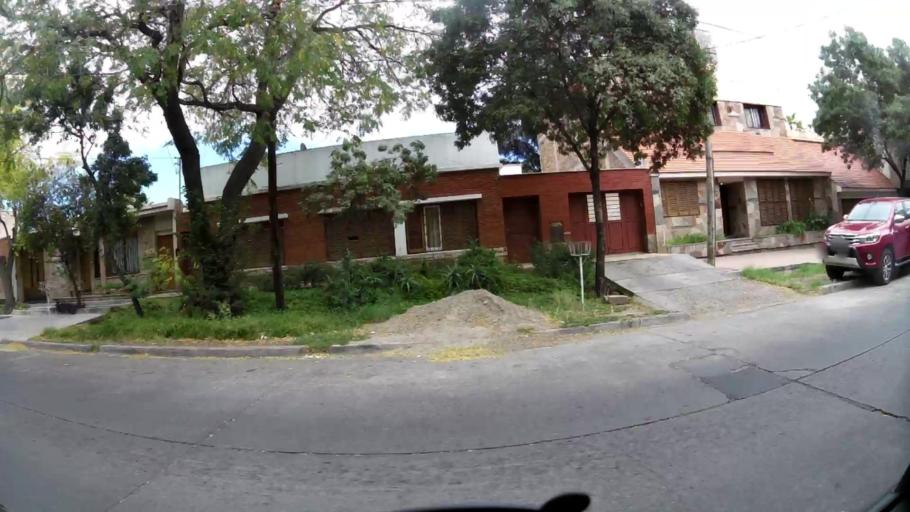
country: AR
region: Mendoza
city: Las Heras
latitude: -32.8671
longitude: -68.8548
